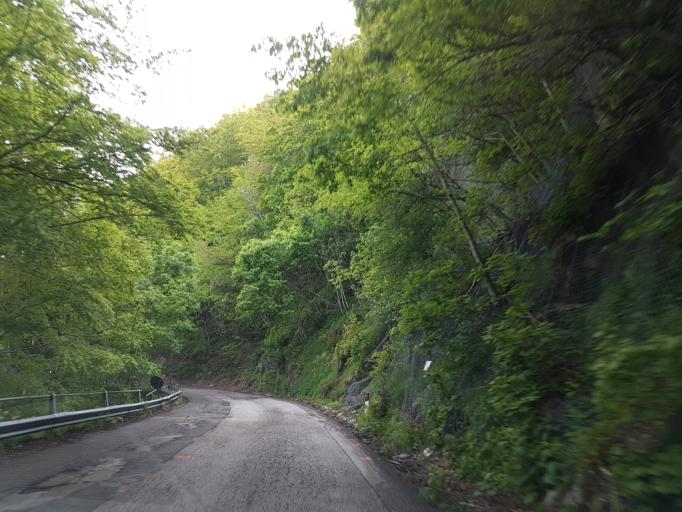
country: IT
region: Emilia-Romagna
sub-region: Forli-Cesena
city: San Piero in Bagno
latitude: 43.8051
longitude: 11.9152
